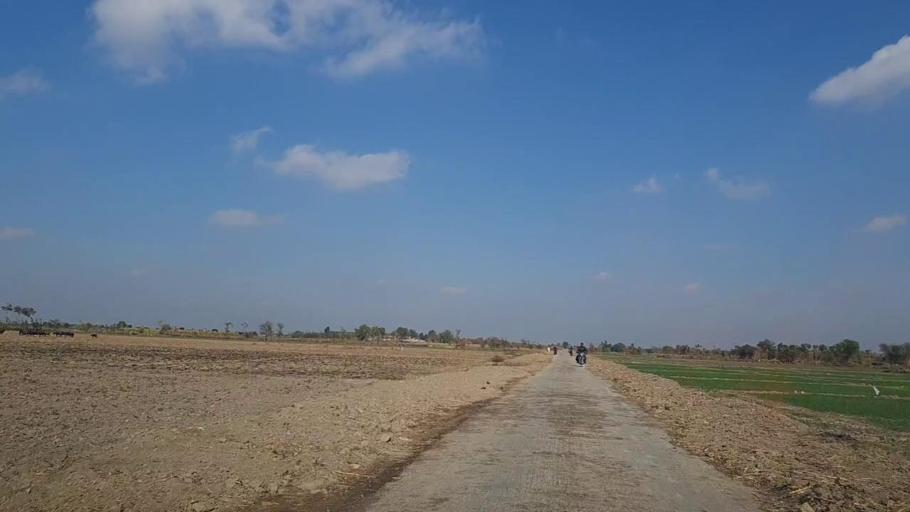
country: PK
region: Sindh
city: Tando Mittha Khan
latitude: 25.9828
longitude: 69.2334
